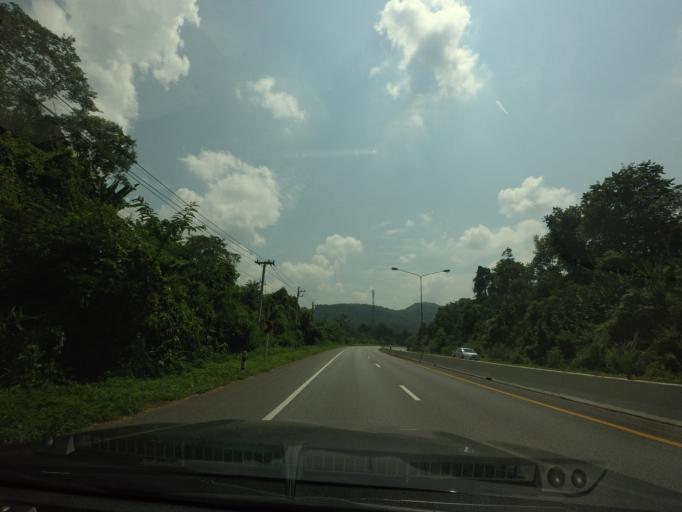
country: TH
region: Uttaradit
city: Lap Lae
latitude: 17.8028
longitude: 100.1133
